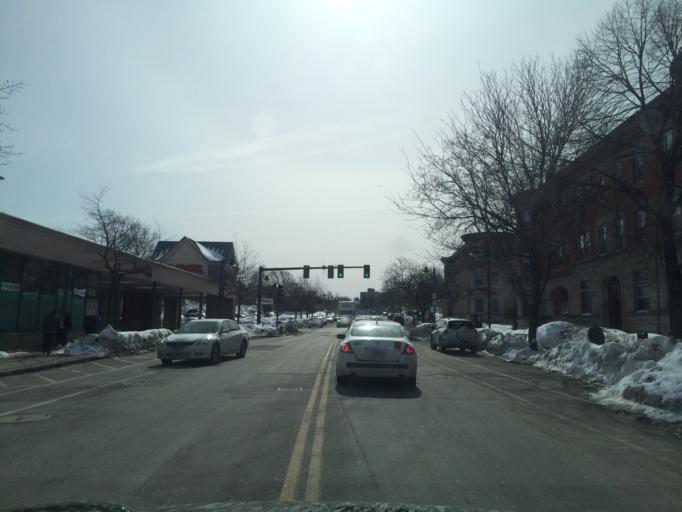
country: US
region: Massachusetts
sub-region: Norfolk County
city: Brookline
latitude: 42.3489
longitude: -71.1298
